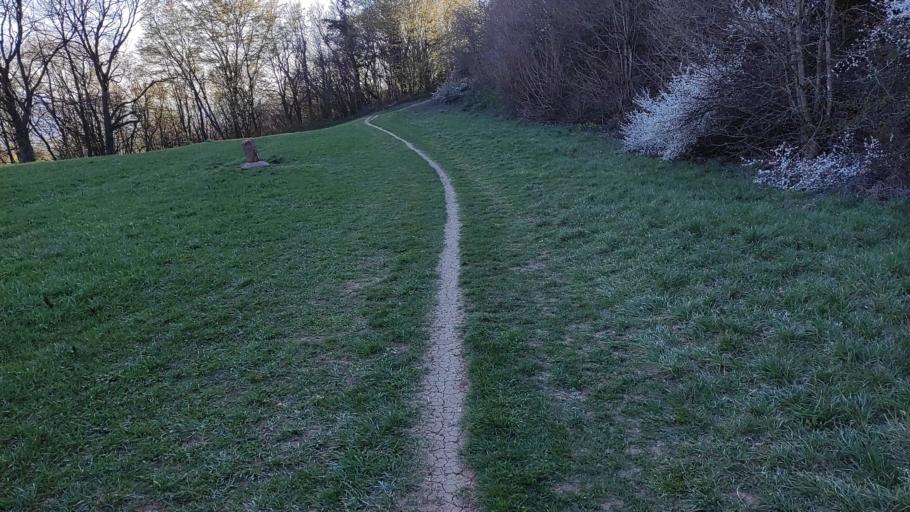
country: DE
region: Baden-Wuerttemberg
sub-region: Freiburg Region
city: Wittnau
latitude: 47.9484
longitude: 7.8030
